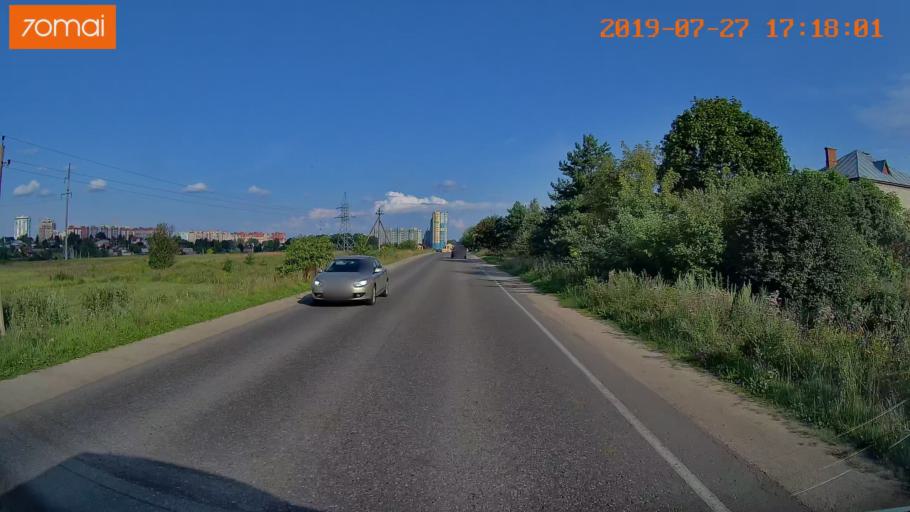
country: RU
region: Ivanovo
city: Novo-Talitsy
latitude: 57.0330
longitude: 40.9017
